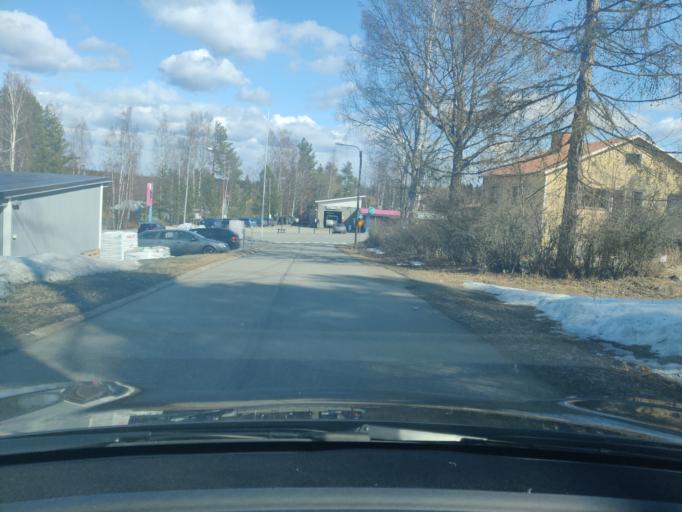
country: FI
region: Northern Savo
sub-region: Kuopio
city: Vehmersalmi
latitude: 62.9136
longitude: 28.1592
